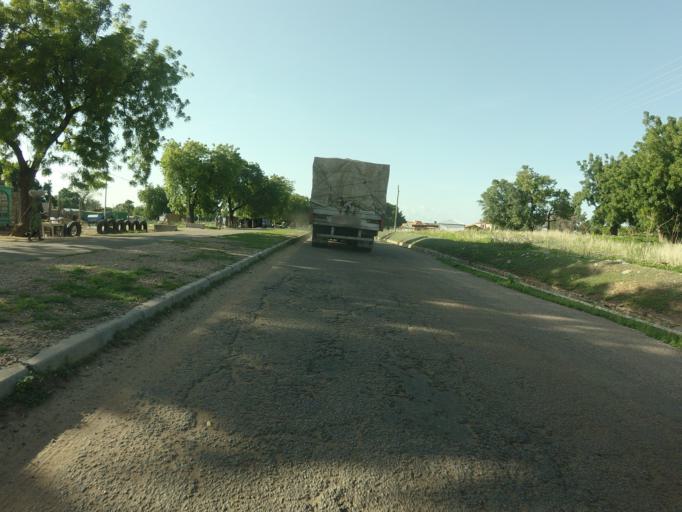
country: GH
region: Upper East
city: Navrongo
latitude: 10.9019
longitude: -1.0920
